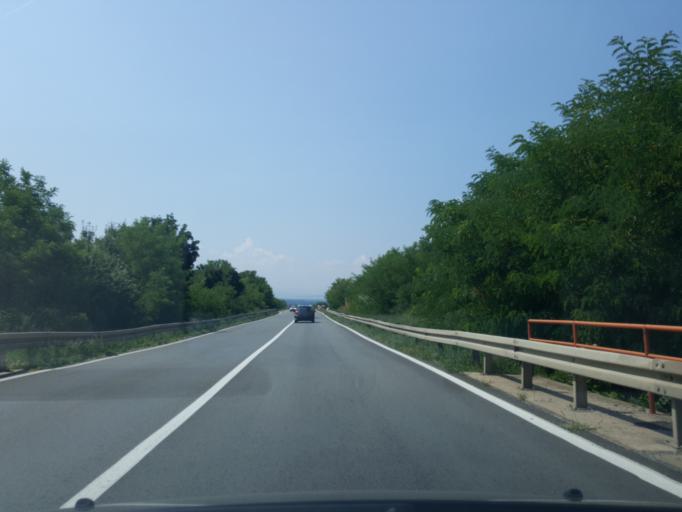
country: RS
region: Central Serbia
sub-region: Belgrade
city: Sopot
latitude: 44.5227
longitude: 20.6543
